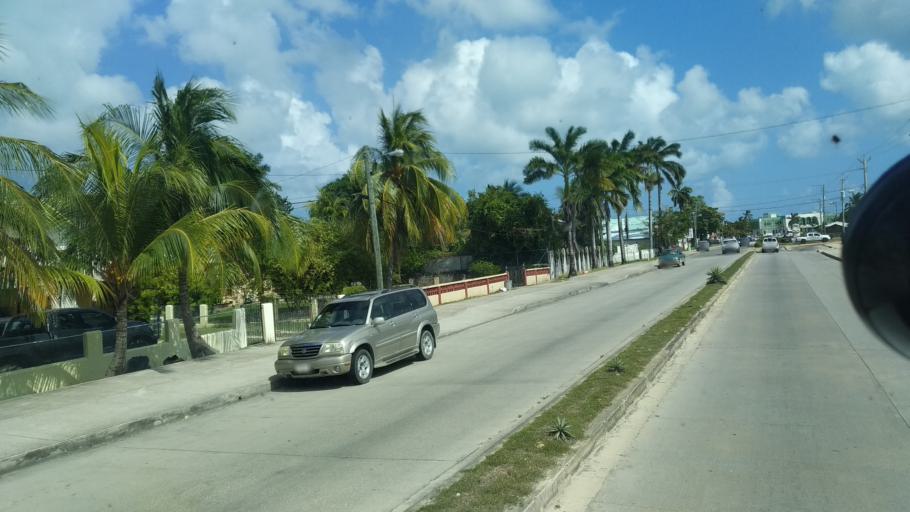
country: BZ
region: Belize
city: Belize City
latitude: 17.5087
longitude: -88.1983
